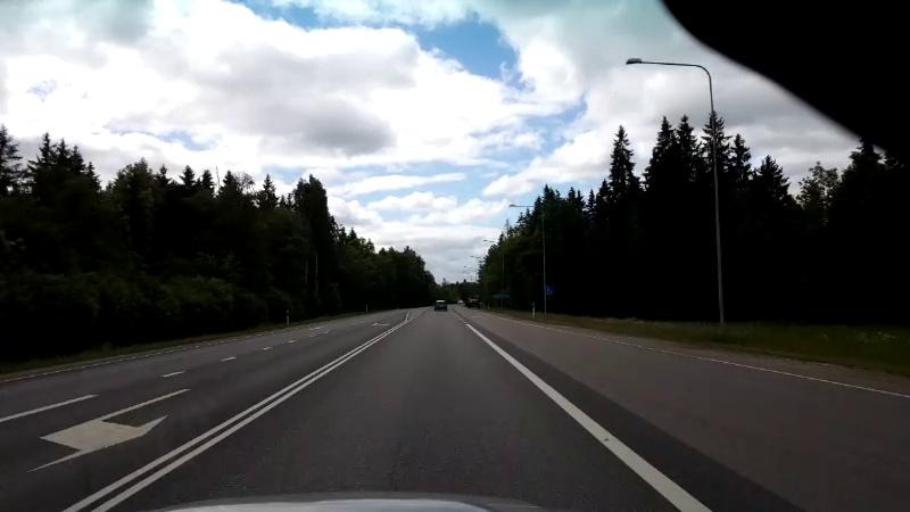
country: EE
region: Paernumaa
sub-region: Halinga vald
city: Parnu-Jaagupi
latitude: 58.6162
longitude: 24.5125
